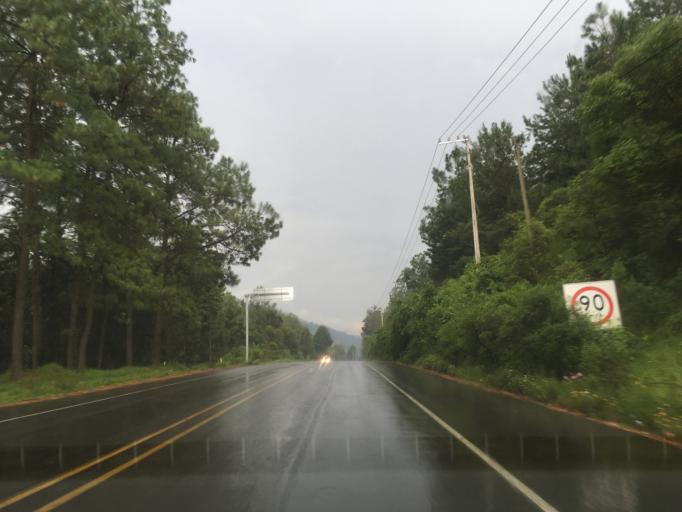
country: MX
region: Michoacan
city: Angahuan
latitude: 19.5635
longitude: -102.2343
